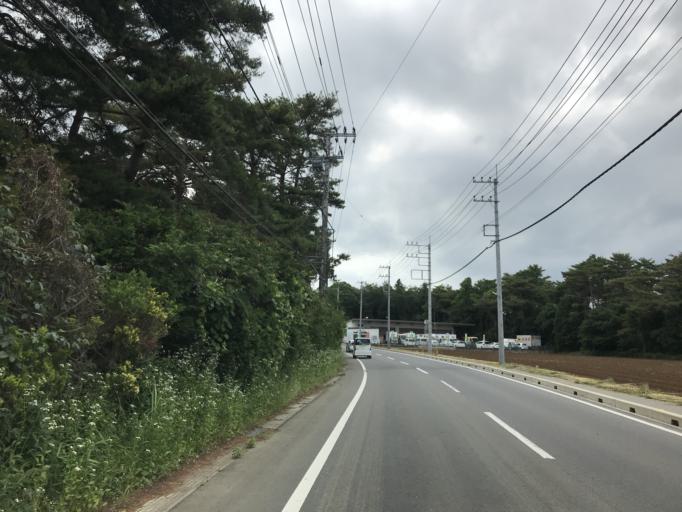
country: JP
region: Ibaraki
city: Ushiku
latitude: 35.9794
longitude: 140.0700
